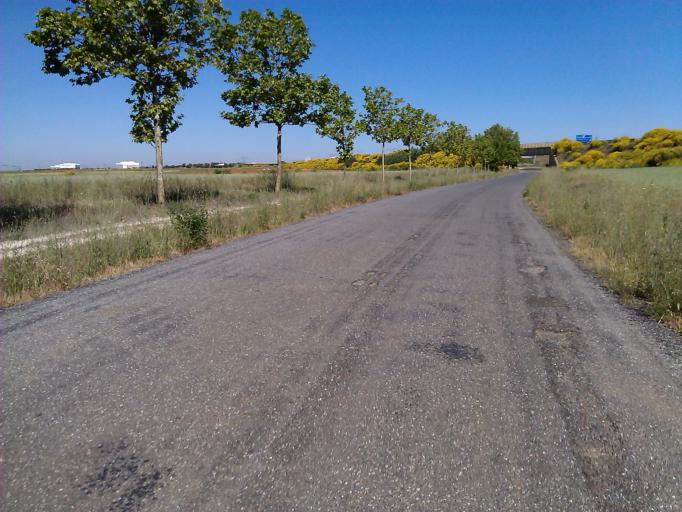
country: ES
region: Castille and Leon
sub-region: Provincia de Leon
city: Vallecillo
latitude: 42.4126
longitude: -5.2011
